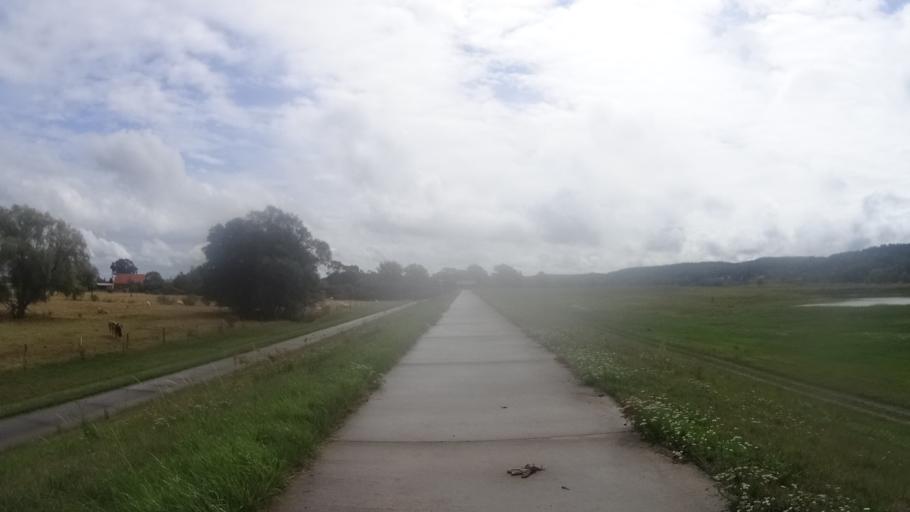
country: DE
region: Lower Saxony
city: Neu Darchau
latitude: 53.2267
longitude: 10.9323
